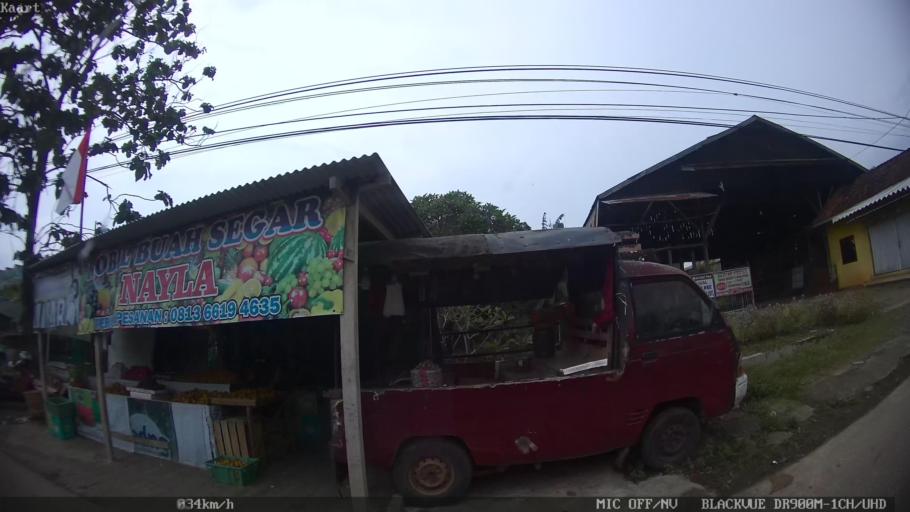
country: ID
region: Lampung
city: Kedaton
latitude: -5.3929
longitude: 105.2278
